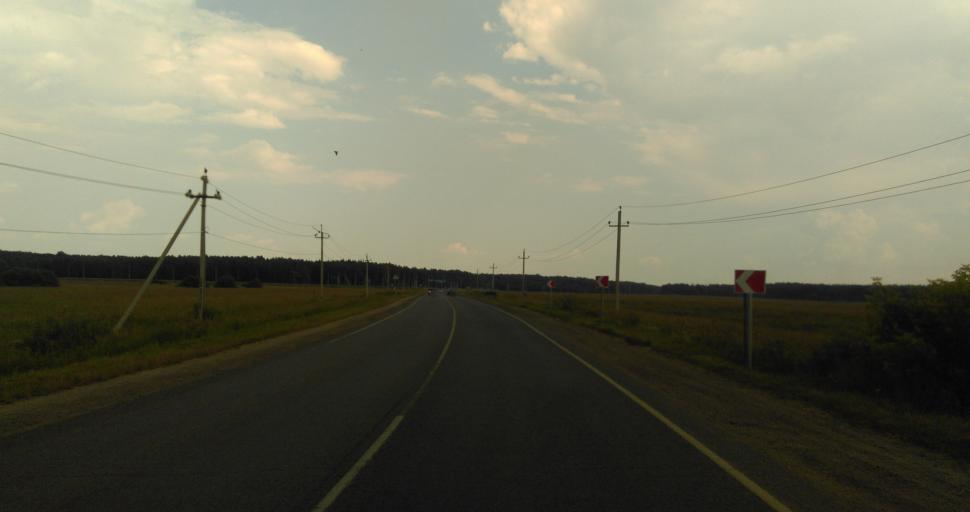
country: RU
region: Moskovskaya
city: Vostryakovo
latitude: 55.3978
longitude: 37.8472
